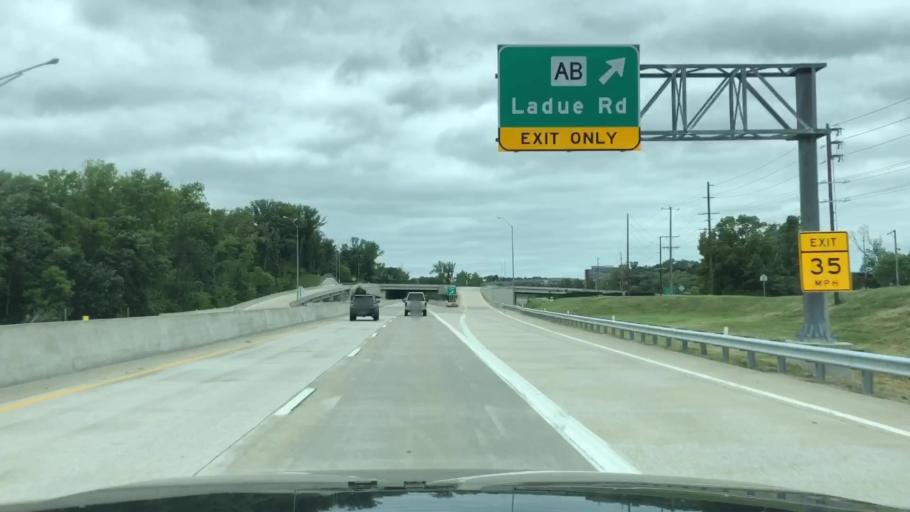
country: US
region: Missouri
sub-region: Saint Louis County
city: Town and Country
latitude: 38.6639
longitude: -90.5021
